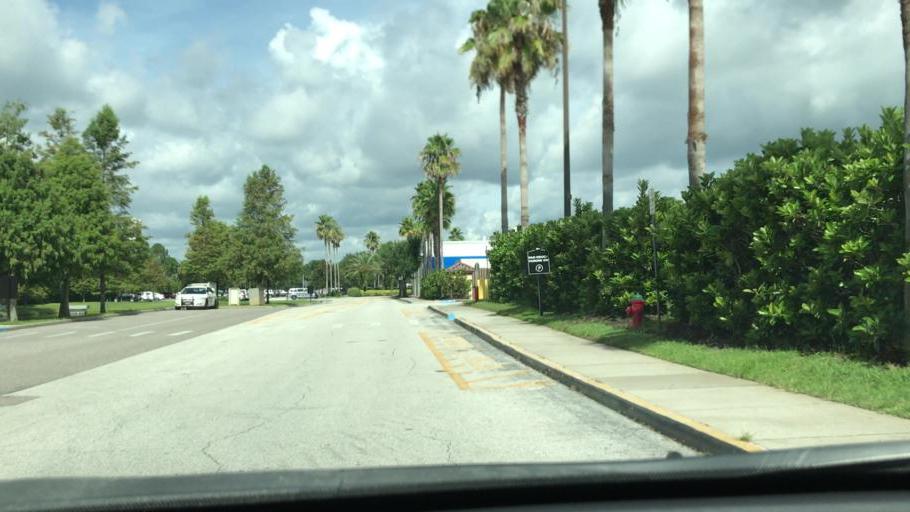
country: US
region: Florida
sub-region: Orange County
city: Williamsburg
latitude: 28.3860
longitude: -81.4925
